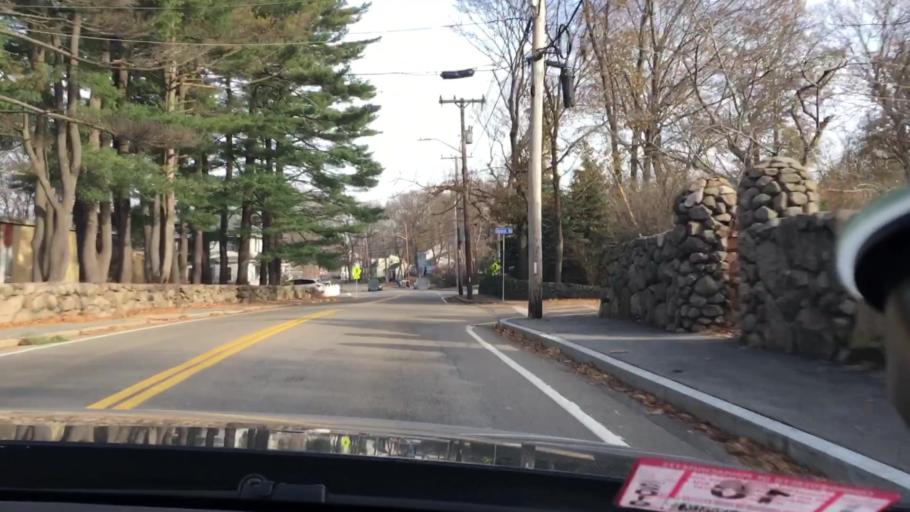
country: US
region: Massachusetts
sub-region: Norfolk County
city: Braintree
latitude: 42.2292
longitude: -71.0032
